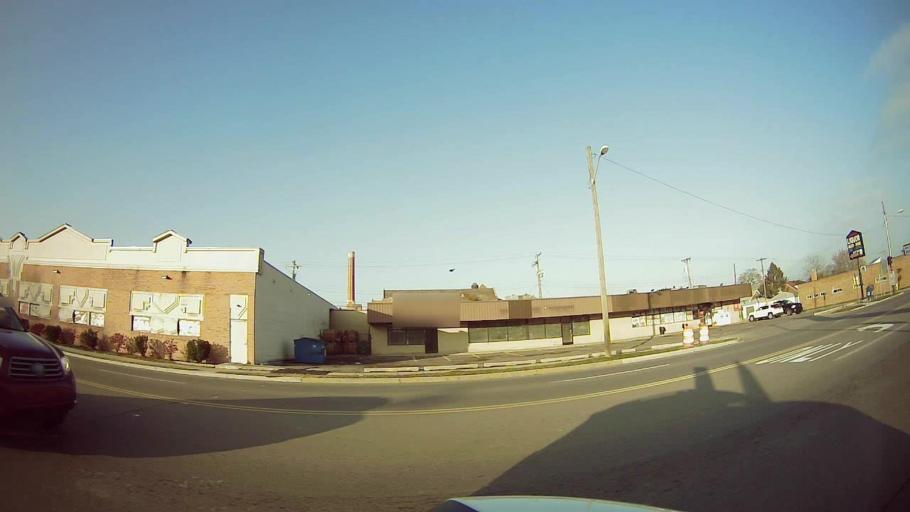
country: US
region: Michigan
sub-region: Wayne County
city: Dearborn
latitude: 42.3482
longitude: -83.1573
